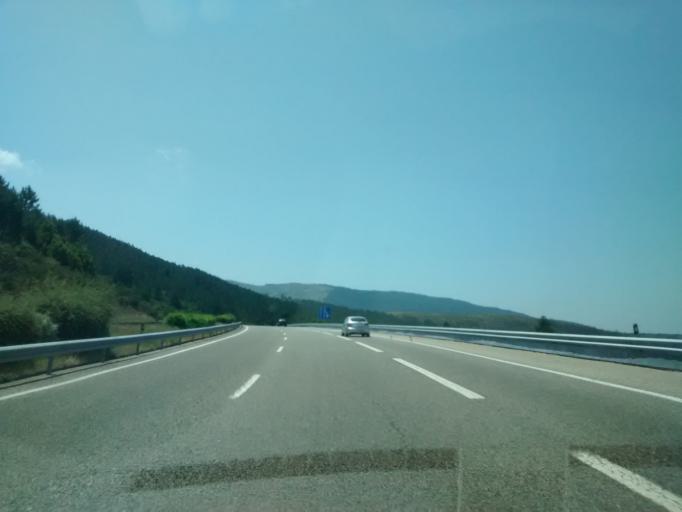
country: PT
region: Viana do Castelo
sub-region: Paredes de Coura
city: Paredes de Coura
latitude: 41.8514
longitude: -8.6224
